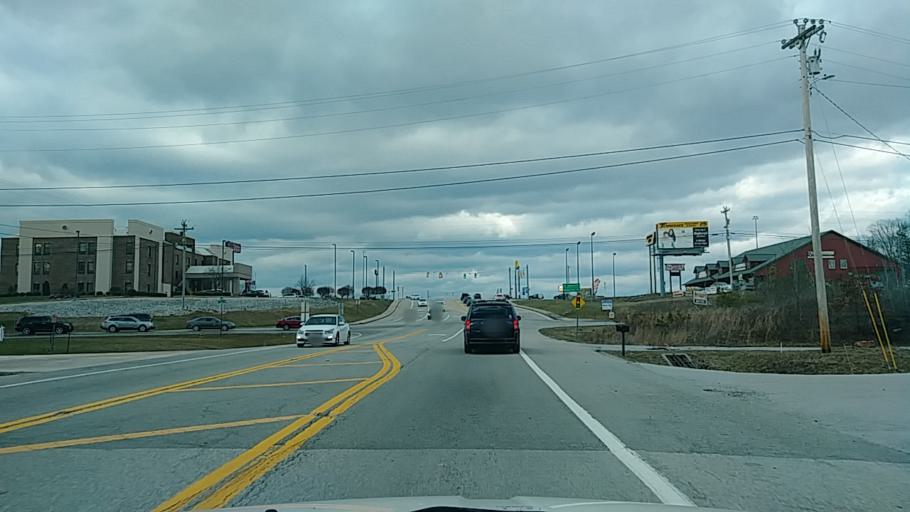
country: US
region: Tennessee
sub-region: Cumberland County
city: Crossville
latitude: 35.9601
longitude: -84.9844
